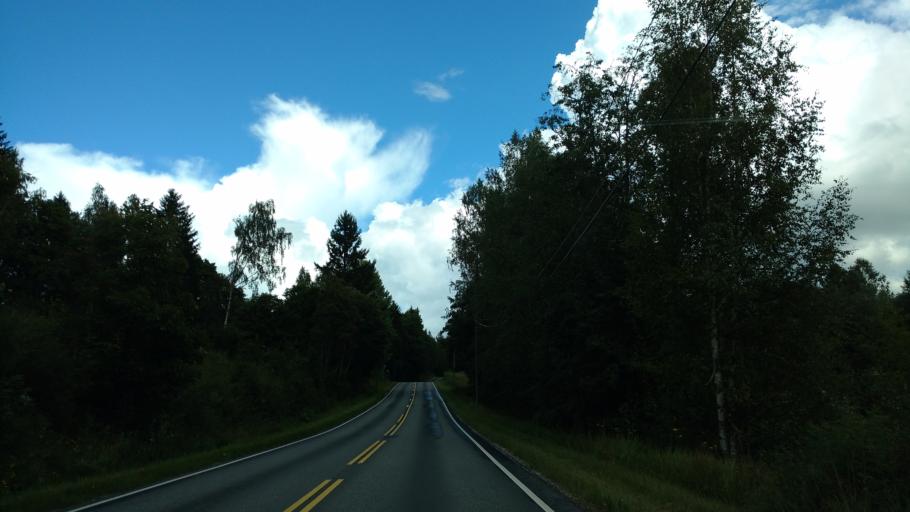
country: FI
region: Uusimaa
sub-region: Helsinki
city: Karjalohja
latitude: 60.2267
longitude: 23.6964
